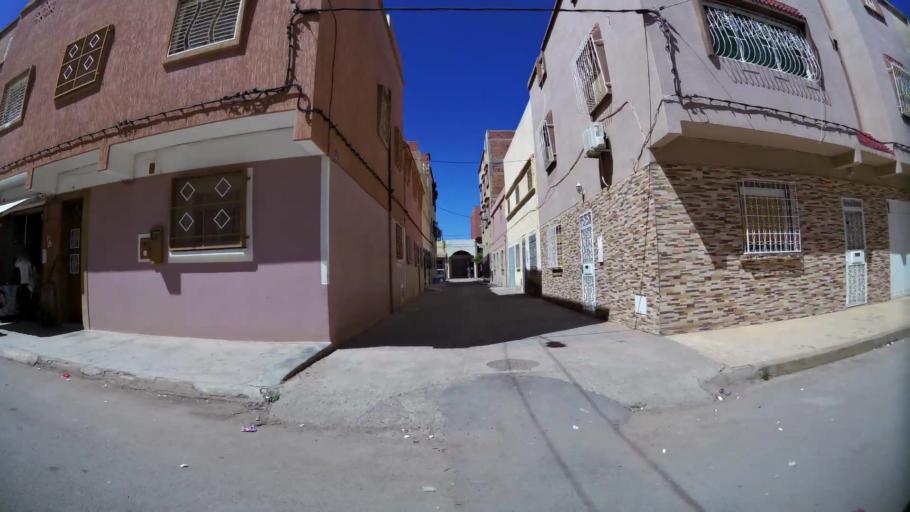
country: MA
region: Oriental
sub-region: Oujda-Angad
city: Oujda
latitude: 34.6690
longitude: -1.9306
